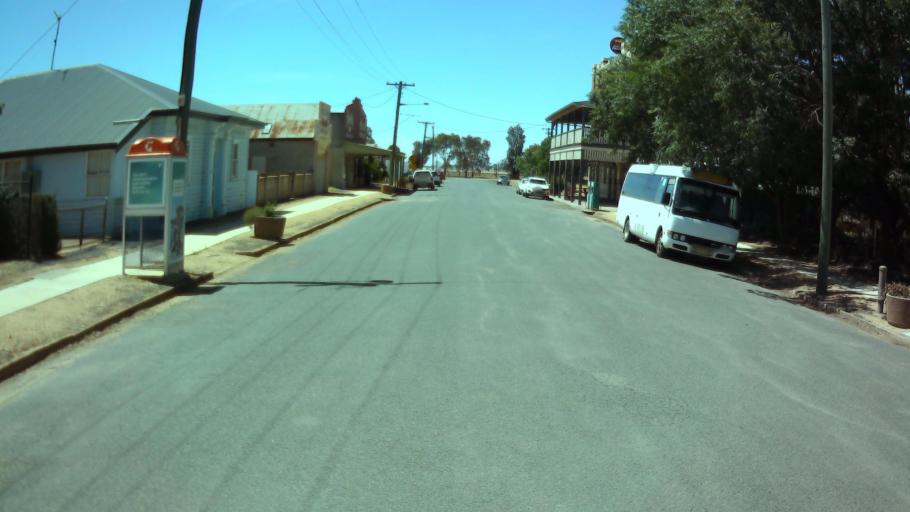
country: AU
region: New South Wales
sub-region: Weddin
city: Grenfell
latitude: -34.0112
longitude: 147.7931
